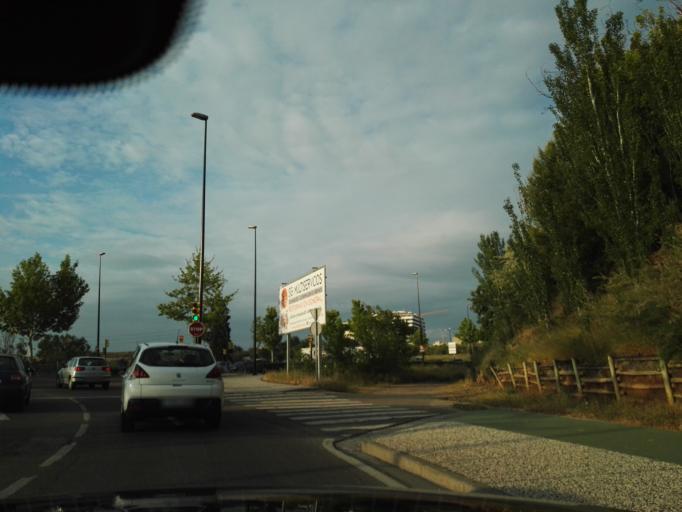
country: ES
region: Aragon
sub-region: Provincia de Zaragoza
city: Zaragoza
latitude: 41.6249
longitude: -0.8692
